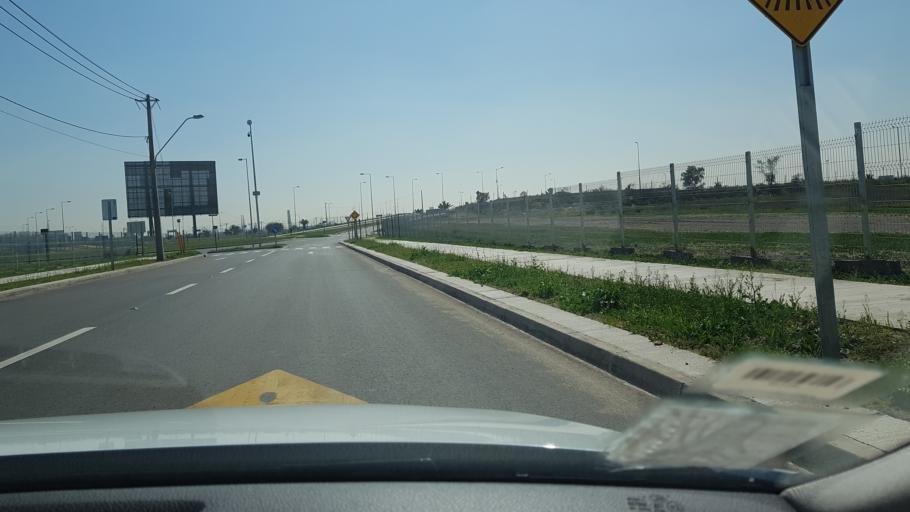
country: CL
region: Santiago Metropolitan
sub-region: Provincia de Santiago
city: Lo Prado
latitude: -33.4242
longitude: -70.7892
